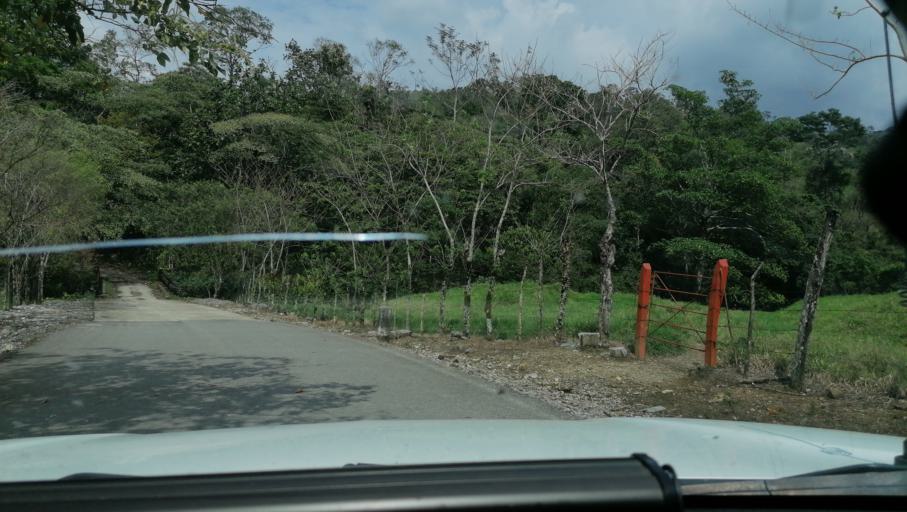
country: MX
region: Chiapas
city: Ocotepec
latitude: 17.3173
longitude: -93.1689
